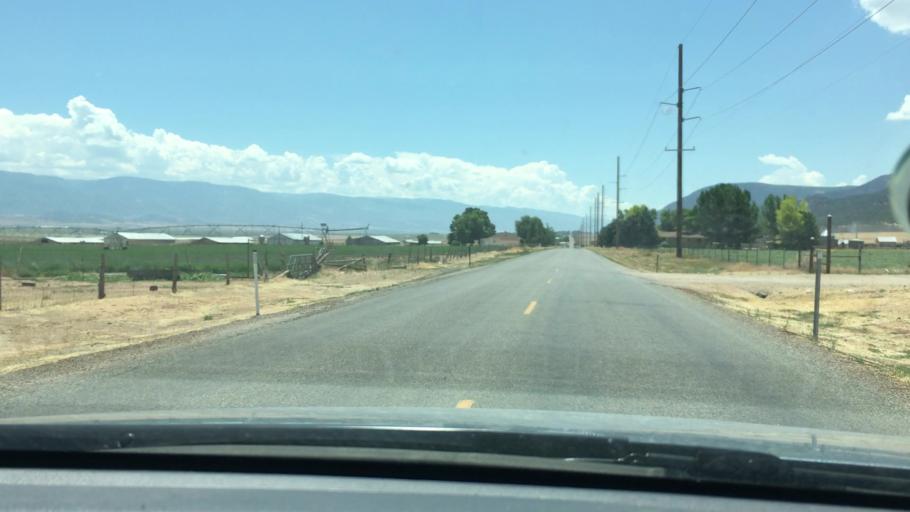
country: US
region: Utah
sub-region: Sanpete County
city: Moroni
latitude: 39.5455
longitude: -111.6400
